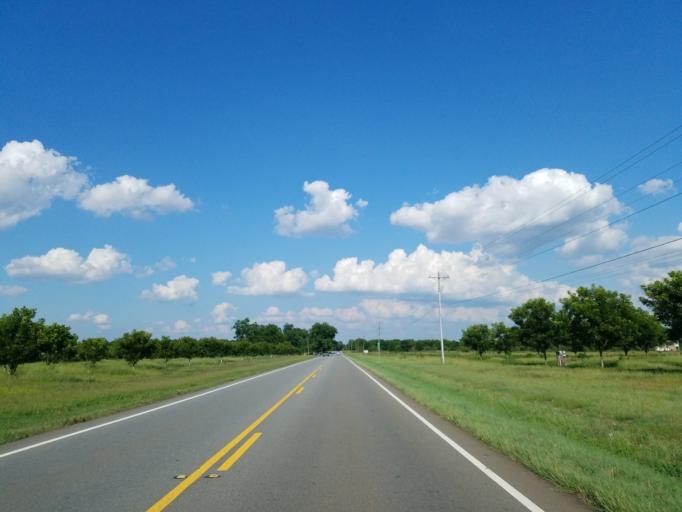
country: US
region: Georgia
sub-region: Peach County
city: Fort Valley
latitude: 32.5538
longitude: -83.7908
